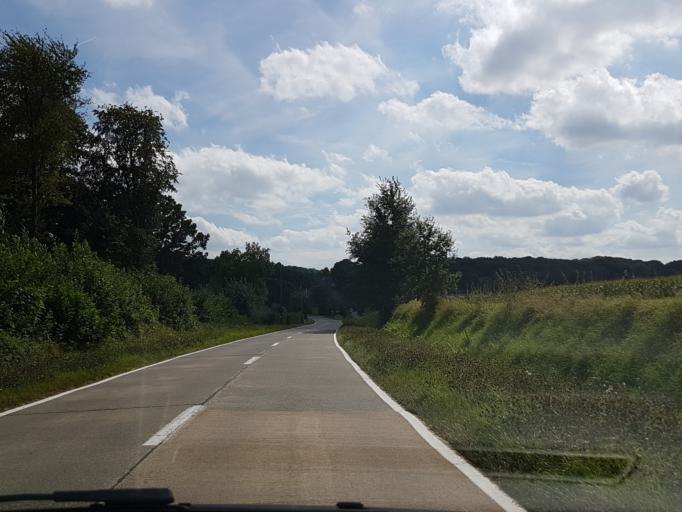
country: BE
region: Flanders
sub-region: Provincie Vlaams-Brabant
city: Bertem
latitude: 50.8887
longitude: 4.6240
